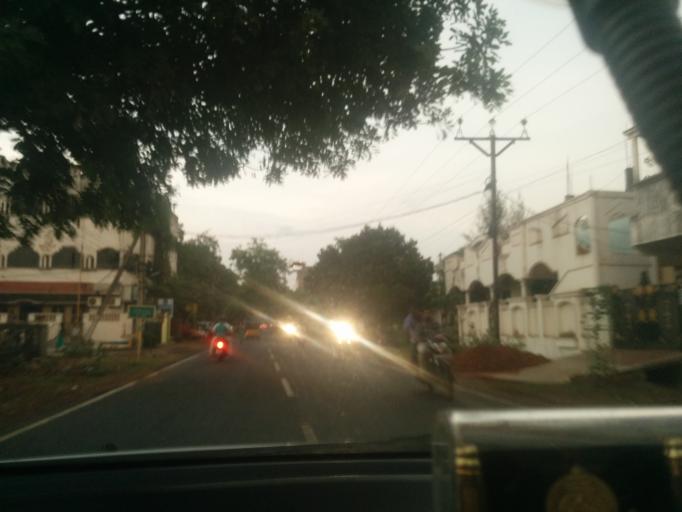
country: IN
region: Andhra Pradesh
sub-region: East Godavari
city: Rajahmundry
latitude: 17.0226
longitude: 81.7933
